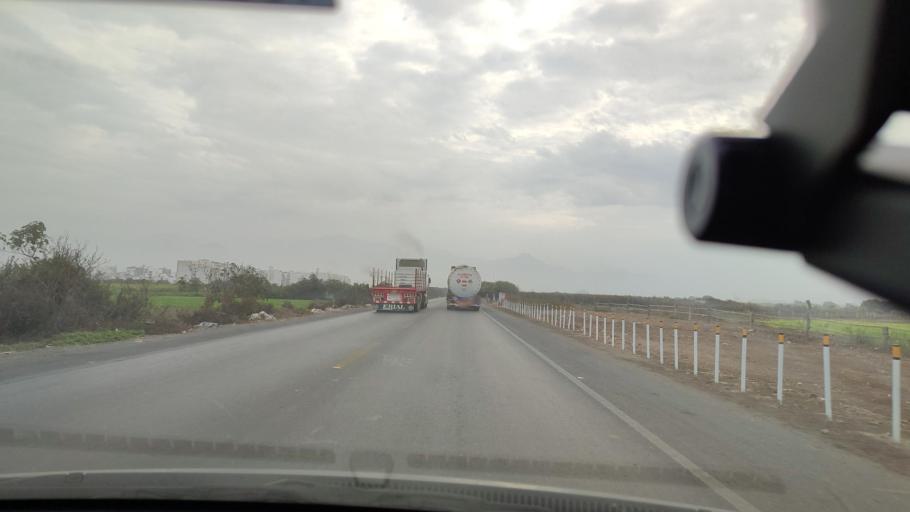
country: PE
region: La Libertad
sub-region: Provincia de Trujillo
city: Buenos Aires
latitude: -8.1502
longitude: -79.0334
